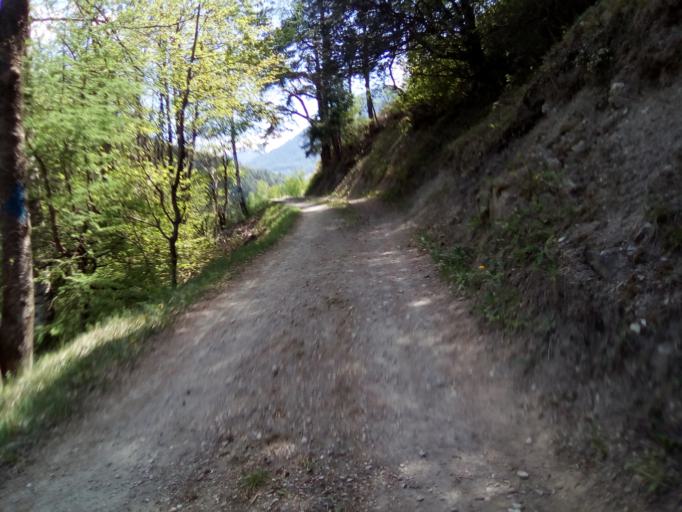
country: CH
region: Valais
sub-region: Entremont District
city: Orsieres
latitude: 46.0453
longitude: 7.1462
